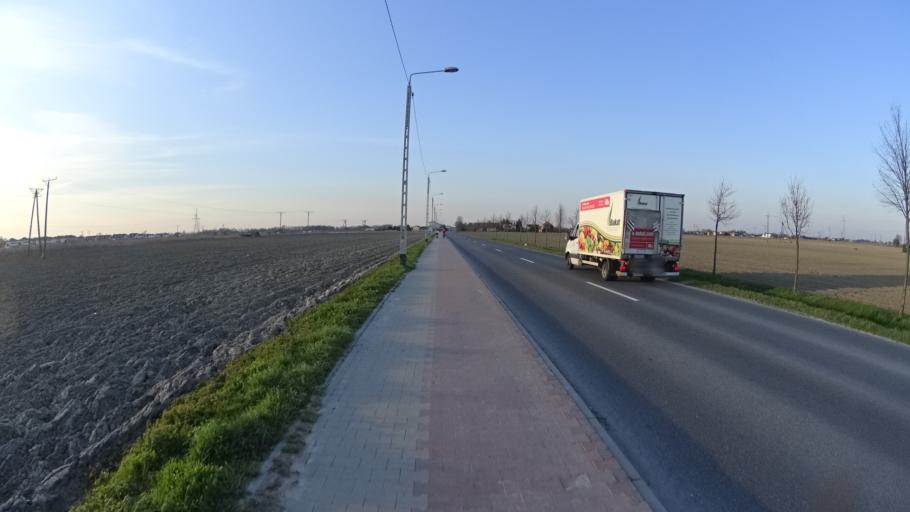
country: PL
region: Masovian Voivodeship
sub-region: Powiat warszawski zachodni
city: Ozarow Mazowiecki
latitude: 52.2174
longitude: 20.8120
